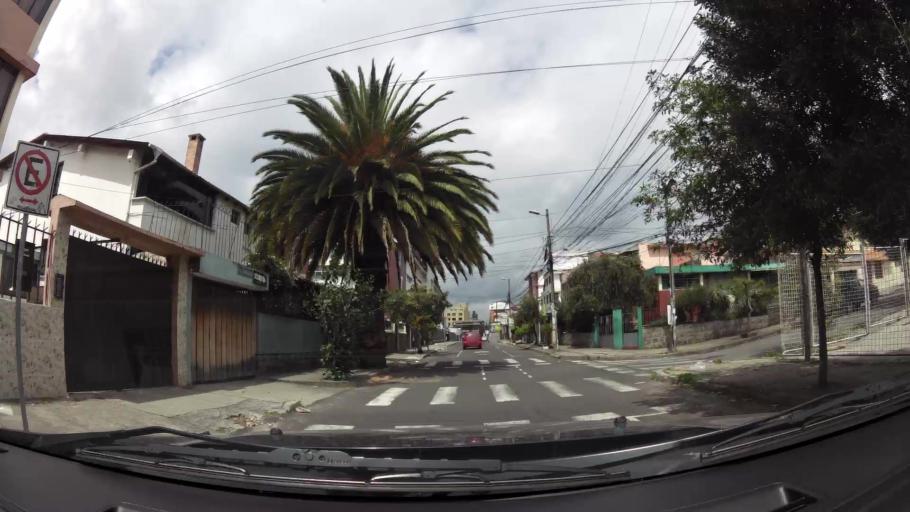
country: EC
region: Pichincha
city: Quito
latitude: -0.1824
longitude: -78.4933
